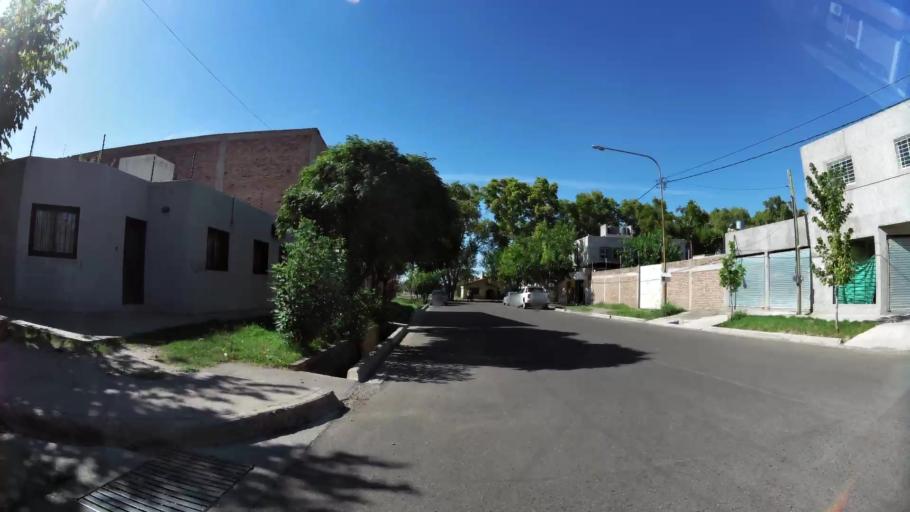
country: AR
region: Mendoza
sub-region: Departamento de Godoy Cruz
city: Godoy Cruz
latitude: -32.9451
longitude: -68.8140
